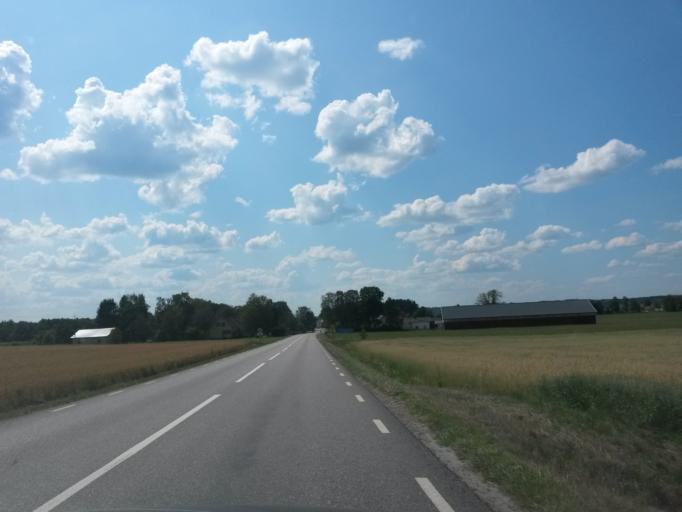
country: SE
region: Vaestra Goetaland
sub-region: Herrljunga Kommun
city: Herrljunga
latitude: 58.0633
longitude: 12.9428
